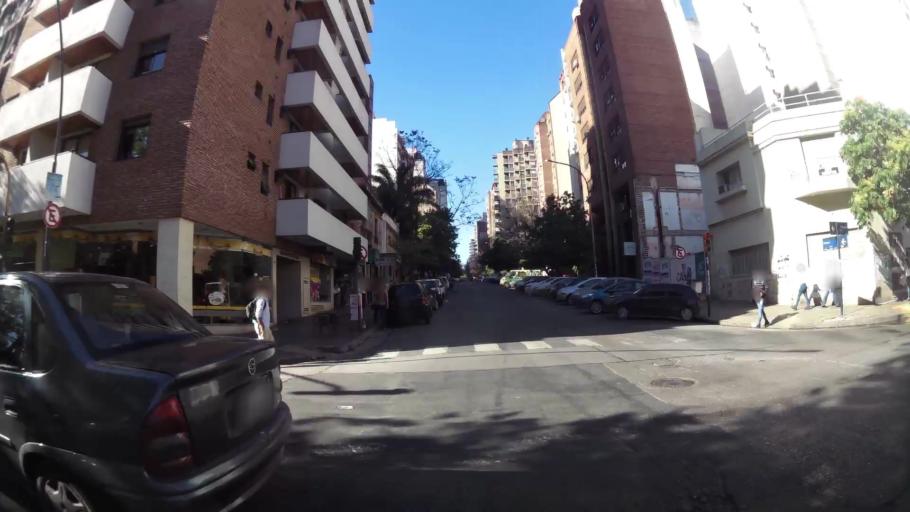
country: AR
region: Cordoba
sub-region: Departamento de Capital
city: Cordoba
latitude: -31.4228
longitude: -64.1796
